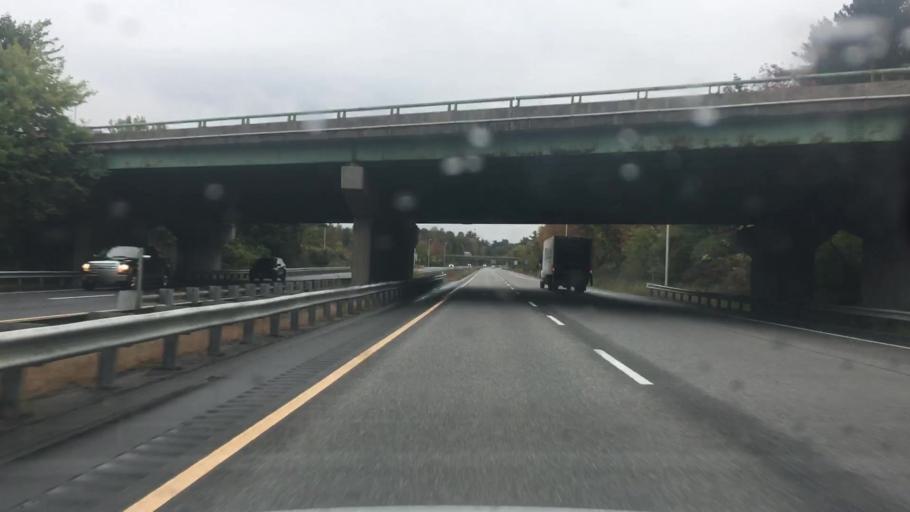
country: US
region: Maine
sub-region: Kennebec County
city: Augusta
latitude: 44.3162
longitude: -69.8114
